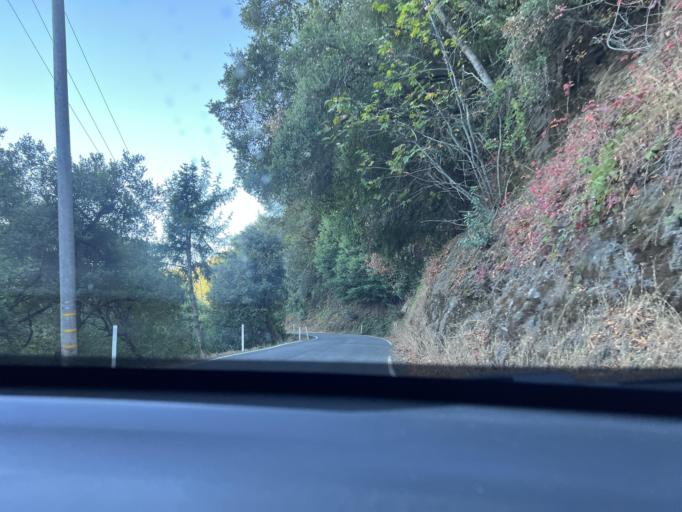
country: US
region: California
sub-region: Santa Clara County
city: Loyola
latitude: 37.2947
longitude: -122.1037
